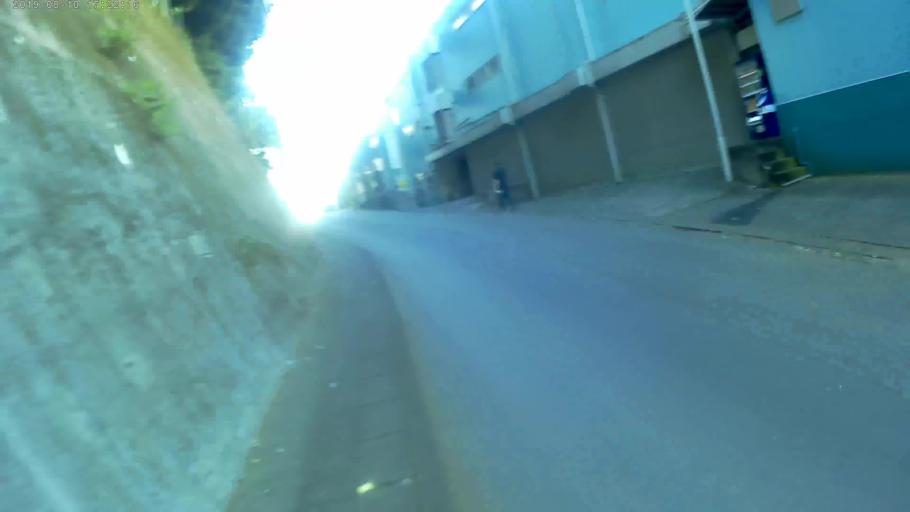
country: JP
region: Yamanashi
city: Uenohara
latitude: 35.6239
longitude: 139.1734
